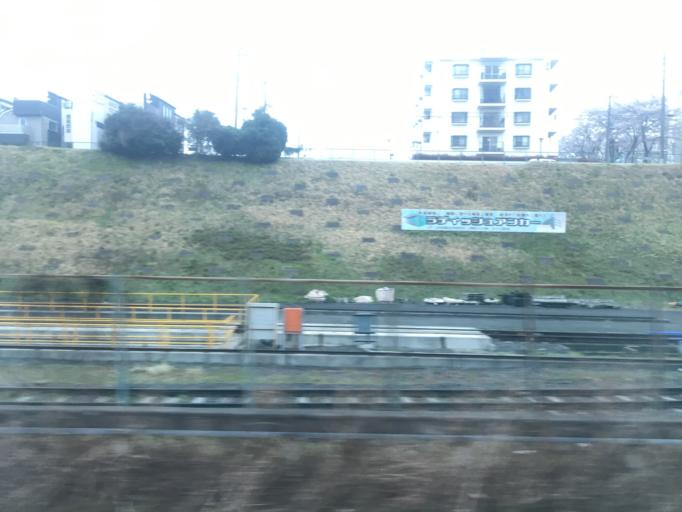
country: JP
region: Tokyo
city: Hino
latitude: 35.6714
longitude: 139.3910
